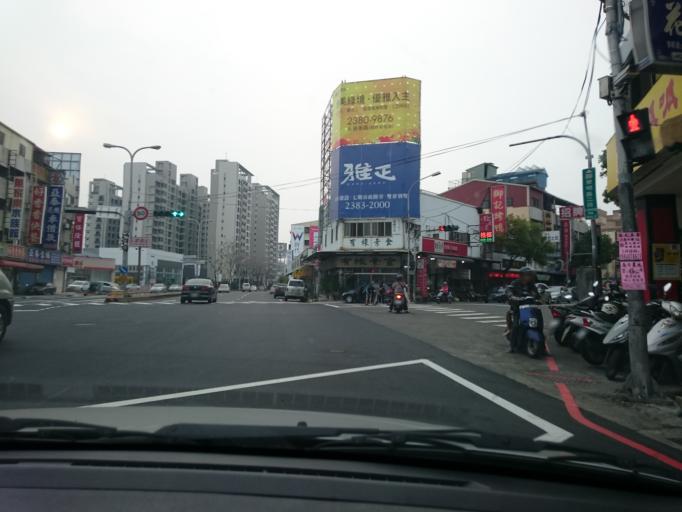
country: TW
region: Taiwan
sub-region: Taichung City
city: Taichung
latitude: 24.1425
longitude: 120.6378
